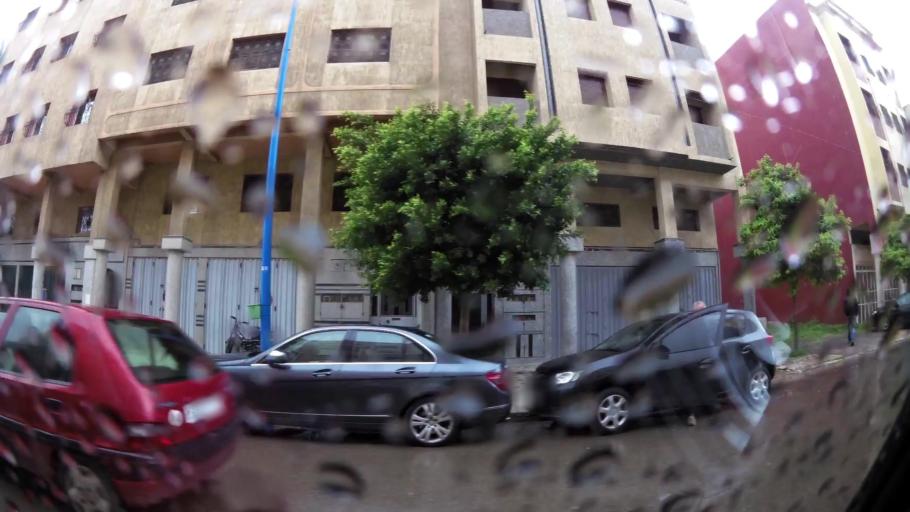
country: MA
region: Grand Casablanca
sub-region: Casablanca
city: Casablanca
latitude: 33.5490
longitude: -7.5553
